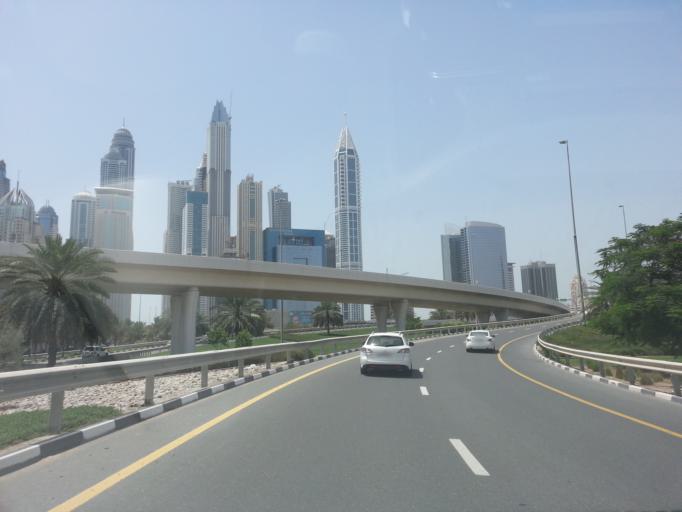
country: AE
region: Dubai
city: Dubai
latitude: 25.0821
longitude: 55.1546
